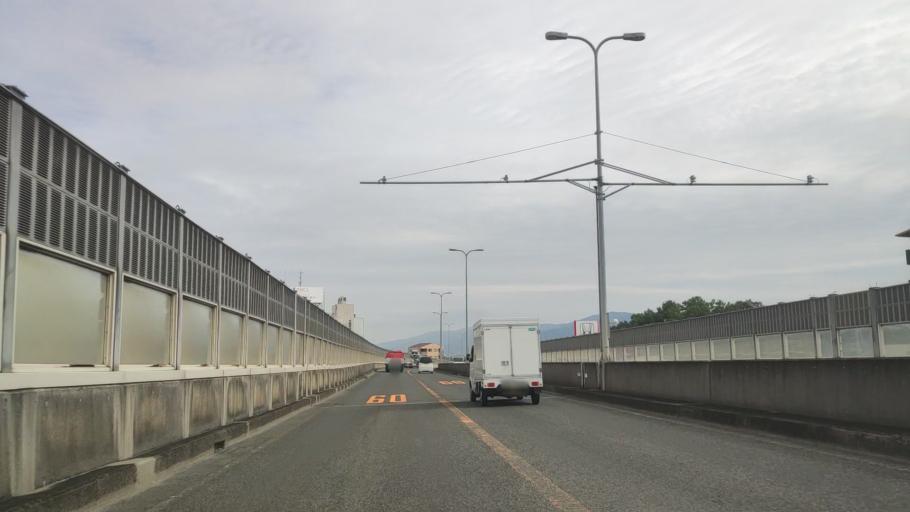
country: JP
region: Osaka
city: Kashihara
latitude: 34.5603
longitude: 135.6005
